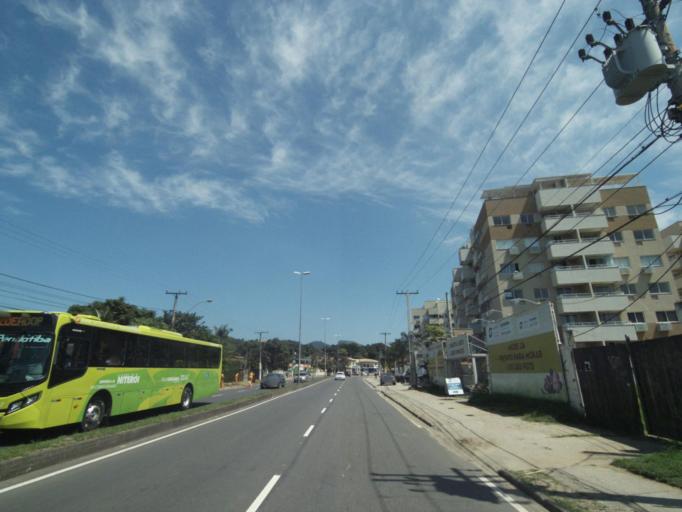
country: BR
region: Rio de Janeiro
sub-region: Sao Goncalo
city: Sao Goncalo
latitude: -22.8833
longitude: -43.0309
